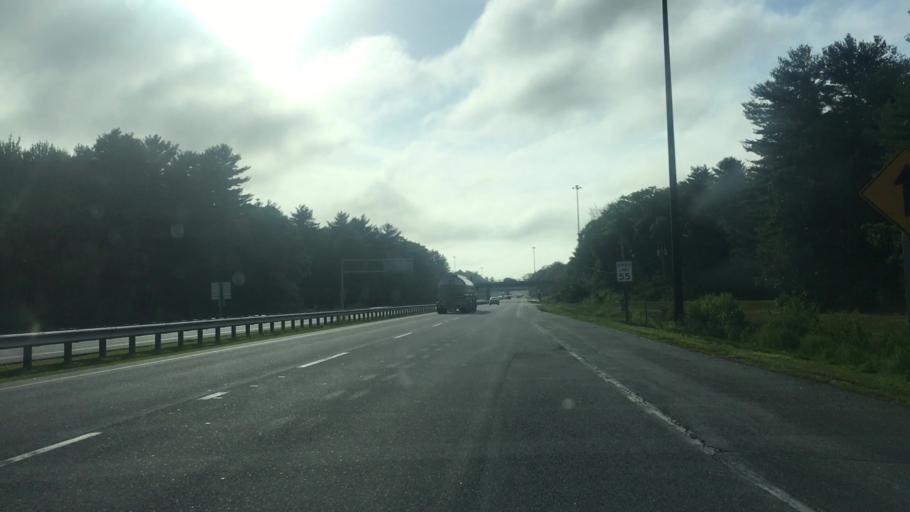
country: US
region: Maine
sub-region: Cumberland County
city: South Portland Gardens
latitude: 43.6246
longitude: -70.3218
